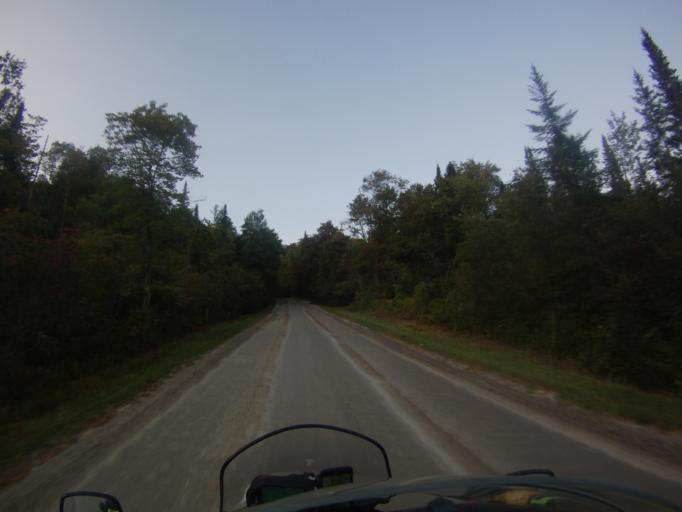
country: US
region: Vermont
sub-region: Addison County
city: Bristol
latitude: 44.0152
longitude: -73.0219
